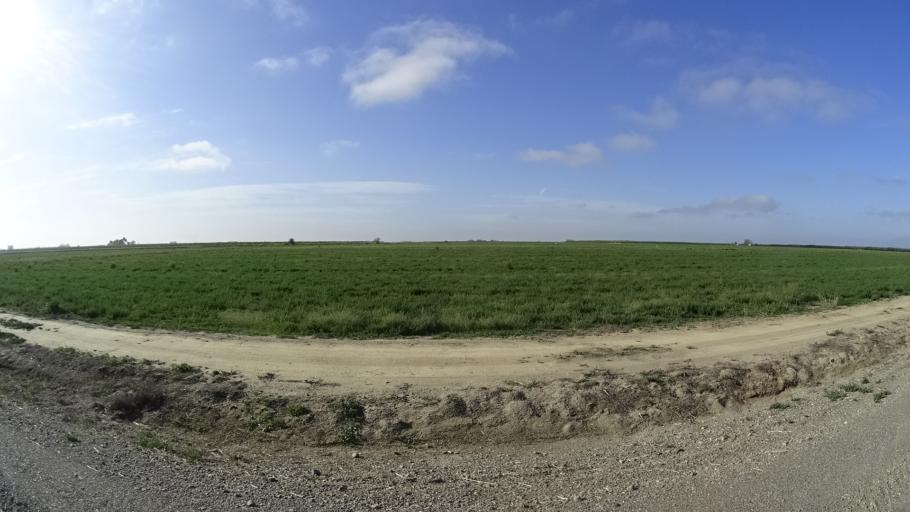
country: US
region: California
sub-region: Glenn County
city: Willows
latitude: 39.5822
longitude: -122.1293
